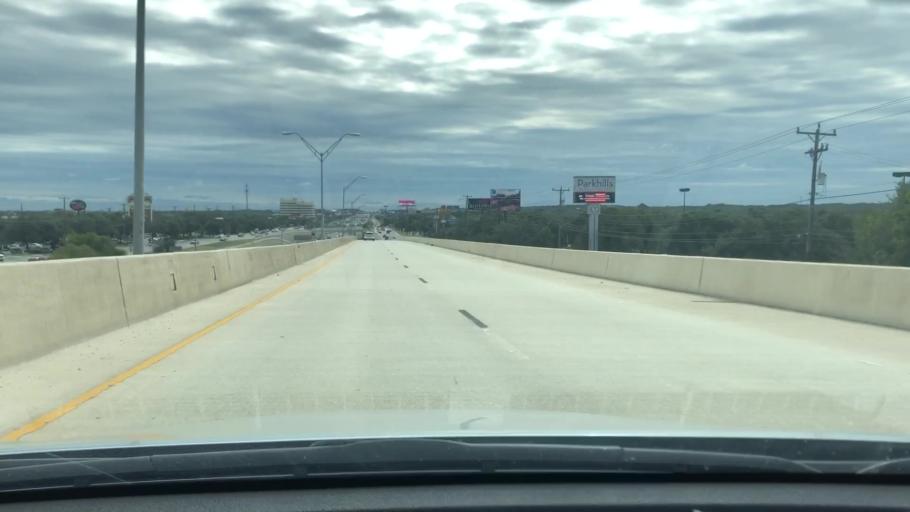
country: US
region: Texas
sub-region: Bexar County
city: Hollywood Park
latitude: 29.6059
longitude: -98.4713
